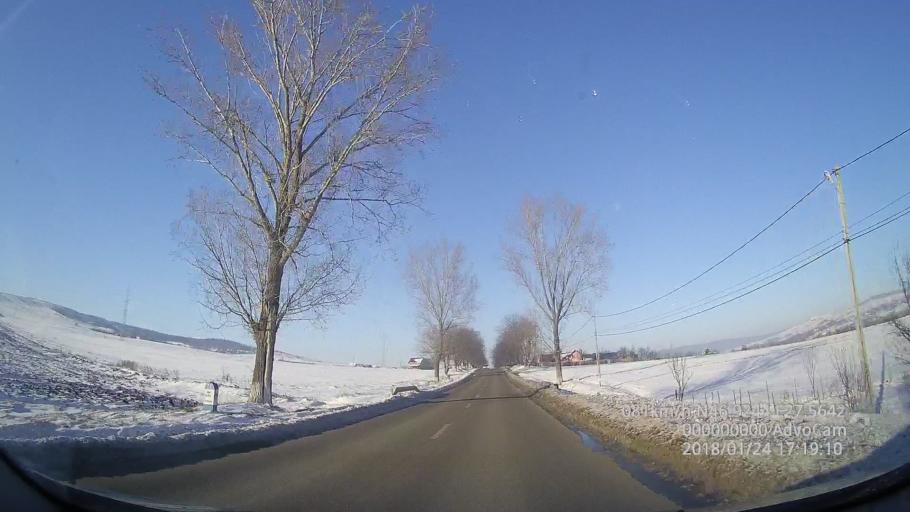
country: RO
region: Iasi
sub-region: Comuna Scanteia
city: Scanteia
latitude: 46.9250
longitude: 27.5641
